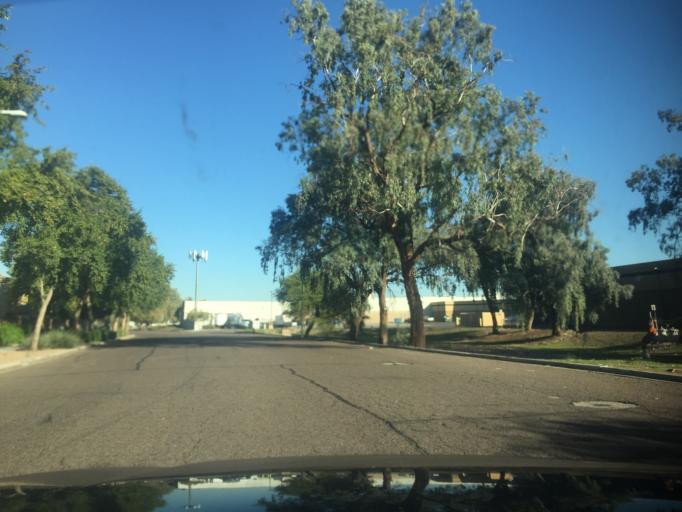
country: US
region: Arizona
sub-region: Maricopa County
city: Tolleson
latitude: 33.4683
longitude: -112.2241
